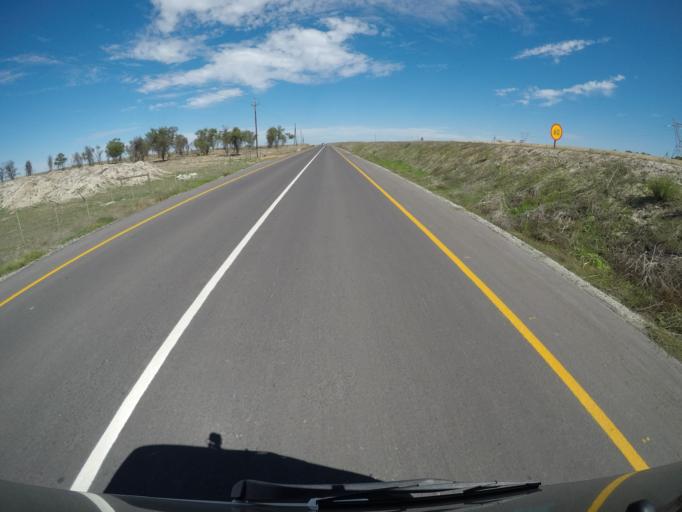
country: ZA
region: Western Cape
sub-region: West Coast District Municipality
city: Malmesbury
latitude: -33.5137
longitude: 18.6569
